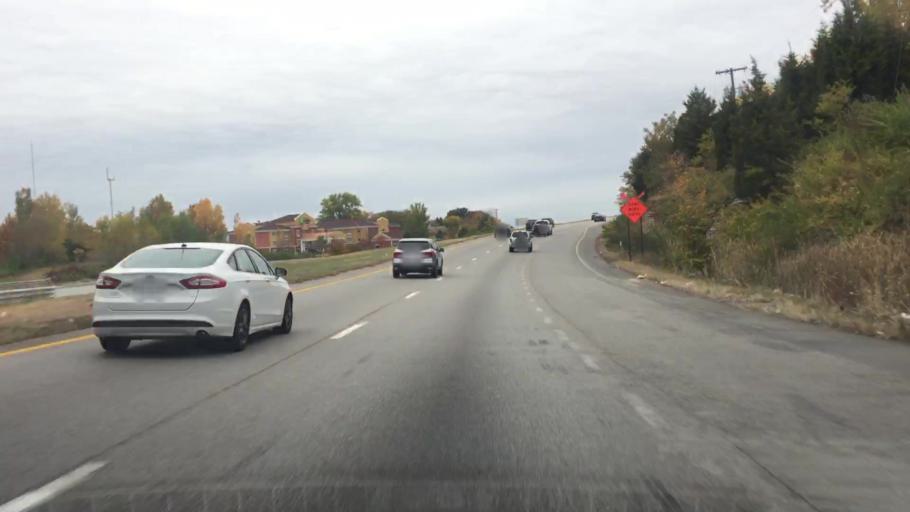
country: US
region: Missouri
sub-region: Jackson County
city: Raytown
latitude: 39.0025
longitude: -94.4841
